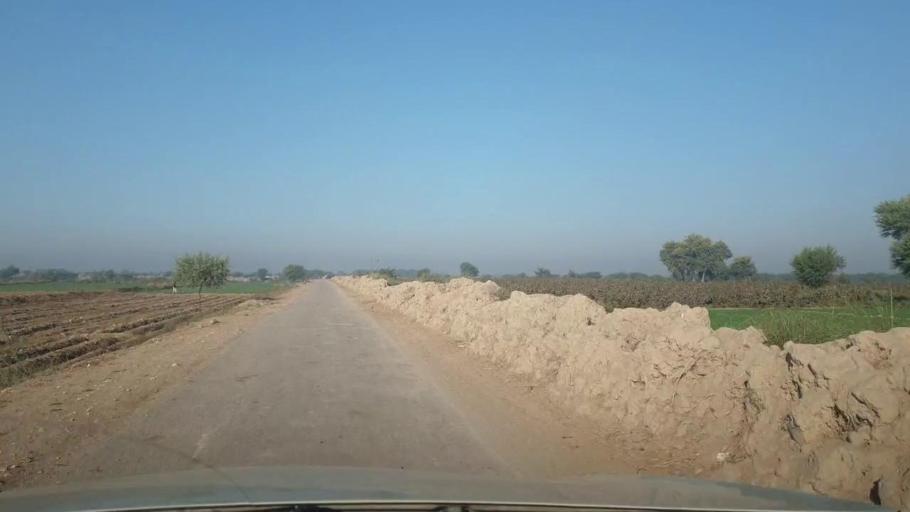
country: PK
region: Sindh
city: Bhan
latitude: 26.5493
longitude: 67.7057
